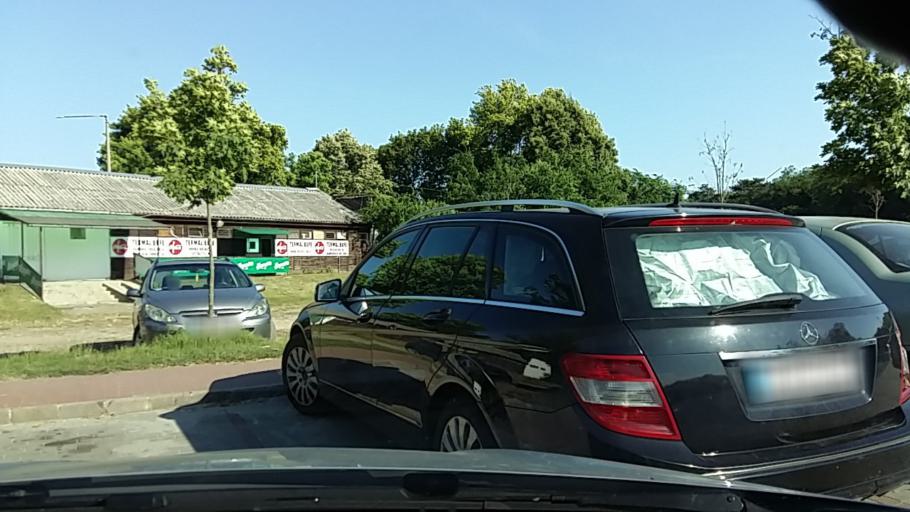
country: HU
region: Pest
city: God
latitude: 47.6923
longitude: 19.1496
